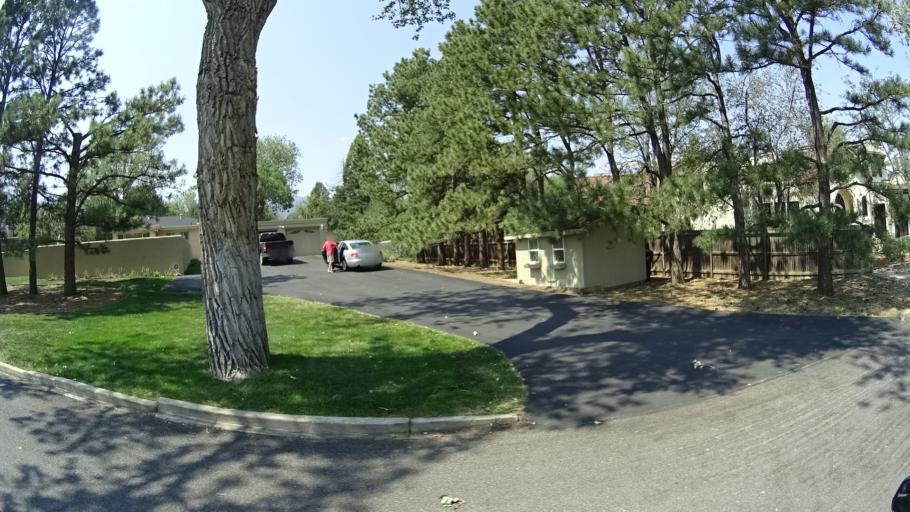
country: US
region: Colorado
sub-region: El Paso County
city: Colorado Springs
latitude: 38.7854
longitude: -104.8429
